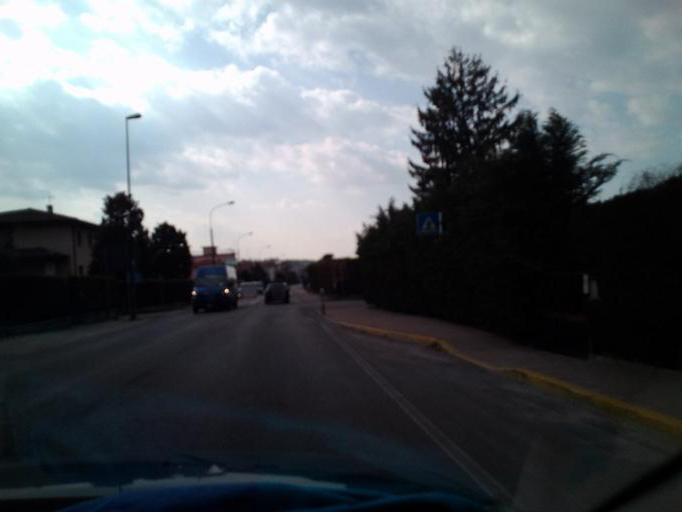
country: IT
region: Veneto
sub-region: Provincia di Verona
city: Arbizzano-Santa Maria
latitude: 45.5026
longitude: 10.9312
